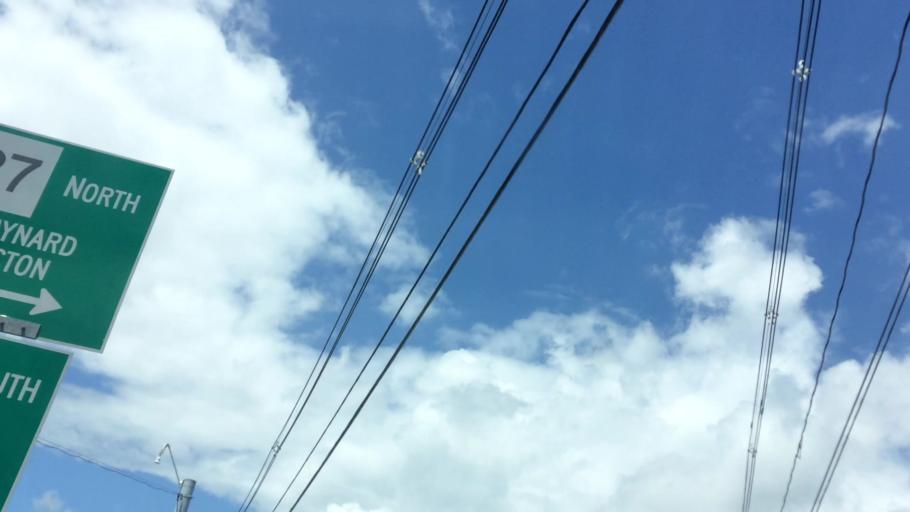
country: US
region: Massachusetts
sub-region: Middlesex County
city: Maynard
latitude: 42.4228
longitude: -71.4478
